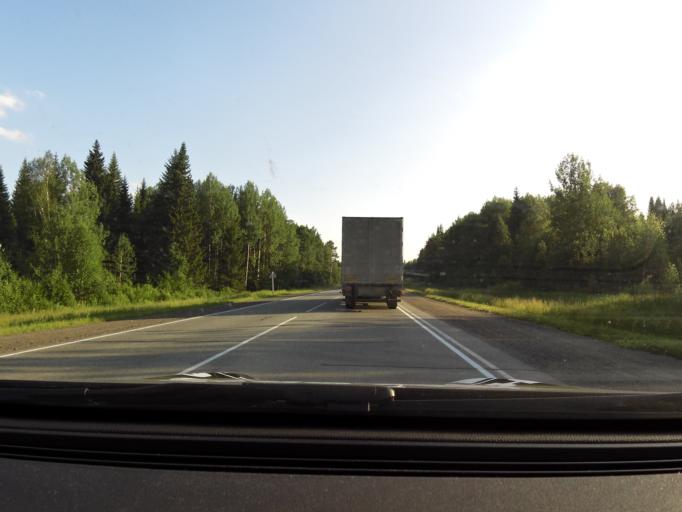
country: RU
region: Sverdlovsk
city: Druzhinino
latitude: 56.7859
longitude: 59.4588
